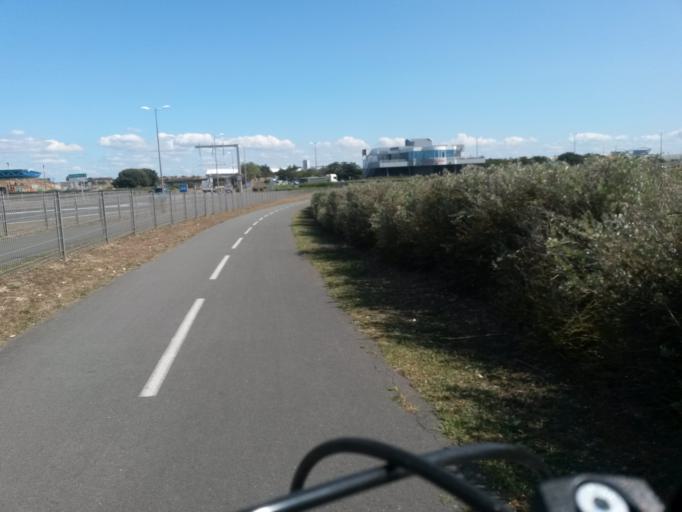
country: FR
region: Poitou-Charentes
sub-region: Departement de la Charente-Maritime
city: Rivedoux-Plage
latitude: 46.1755
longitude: -1.2210
